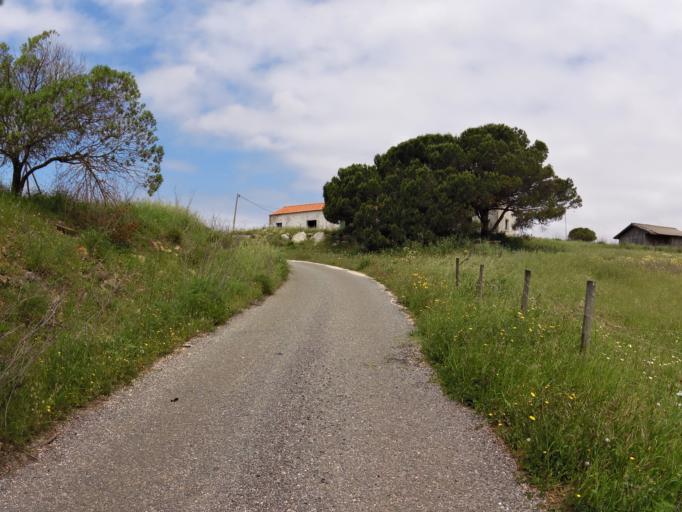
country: PT
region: Faro
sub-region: Vila do Bispo
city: Vila do Bispo
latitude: 37.0785
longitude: -8.8788
